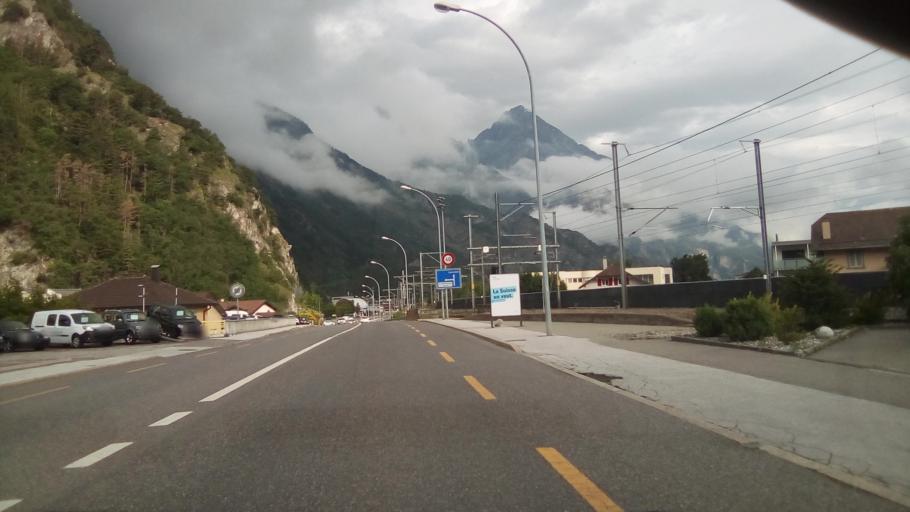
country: CH
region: Valais
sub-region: Martigny District
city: Martigny-Ville
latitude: 46.1067
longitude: 7.0716
